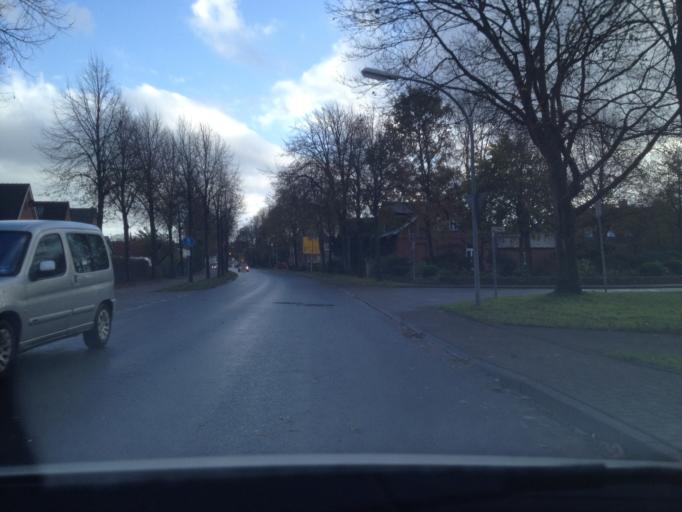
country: DE
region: Schleswig-Holstein
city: Leck
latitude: 54.7760
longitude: 8.9668
